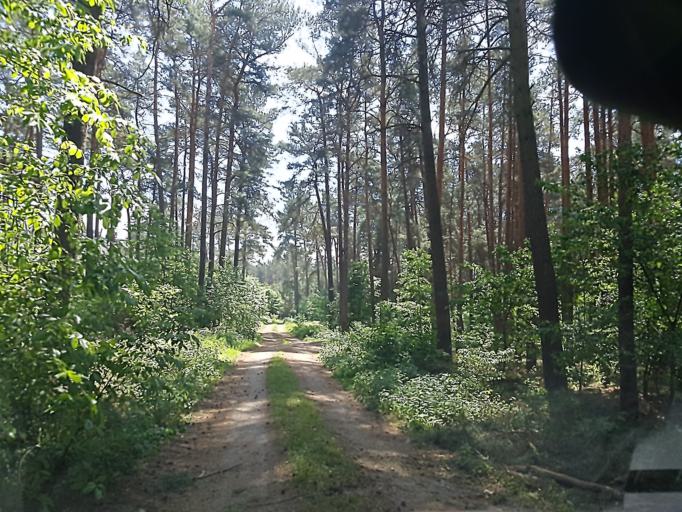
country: DE
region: Brandenburg
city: Gorzke
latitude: 52.1245
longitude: 12.3132
